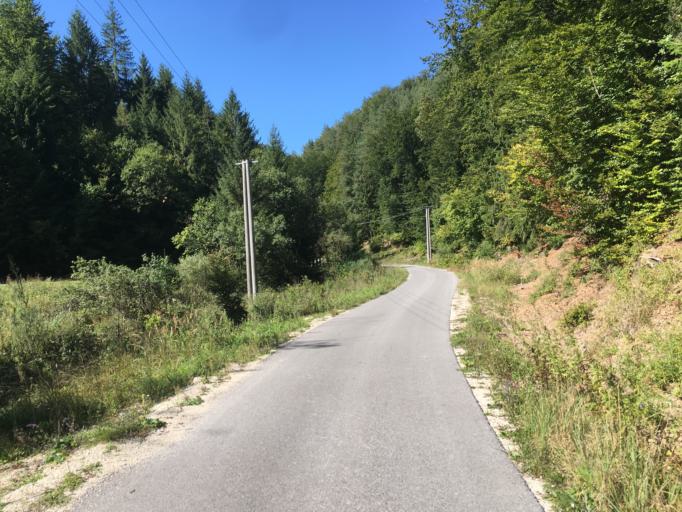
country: SK
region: Trenciansky
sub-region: Okres Povazska Bystrica
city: Povazska Bystrica
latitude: 49.0111
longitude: 18.4488
